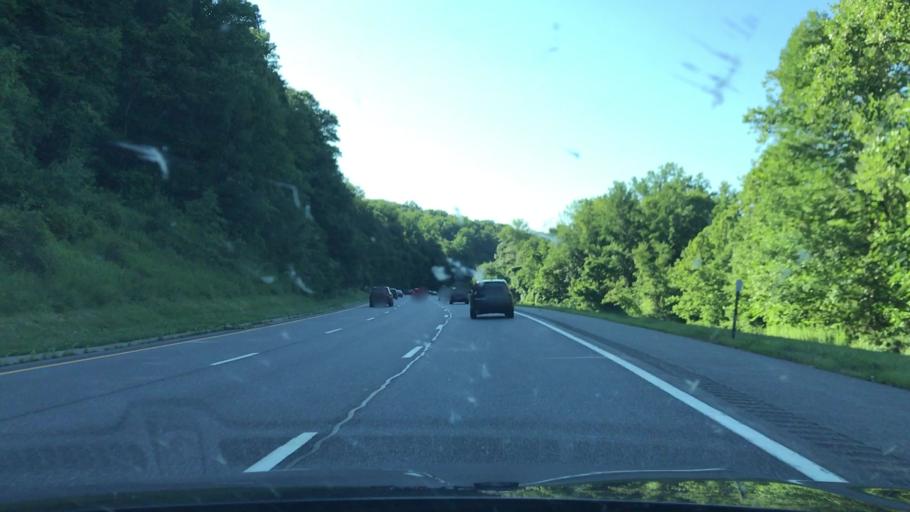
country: US
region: New York
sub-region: Westchester County
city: Yorktown Heights
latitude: 41.2307
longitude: -73.8089
